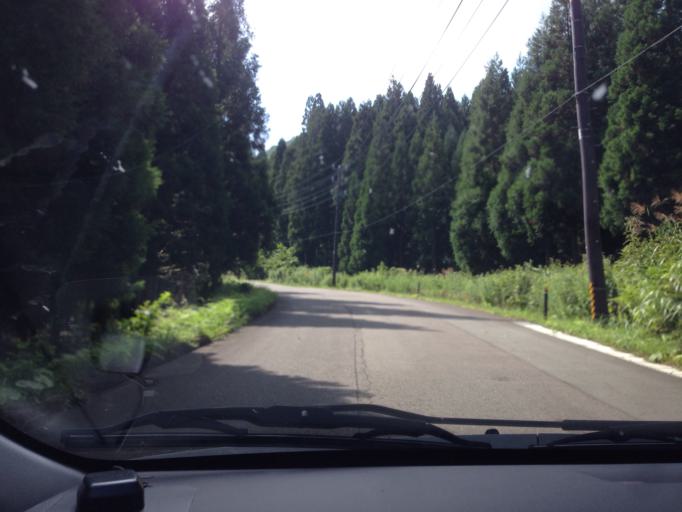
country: JP
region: Fukushima
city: Inawashiro
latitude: 37.3473
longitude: 140.0576
